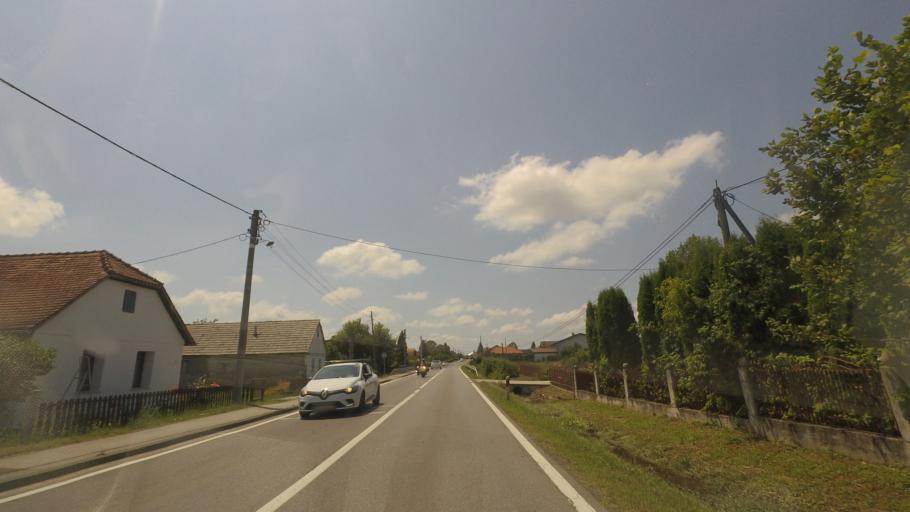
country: HR
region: Zagrebacka
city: Jastrebarsko
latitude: 45.5868
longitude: 15.5960
